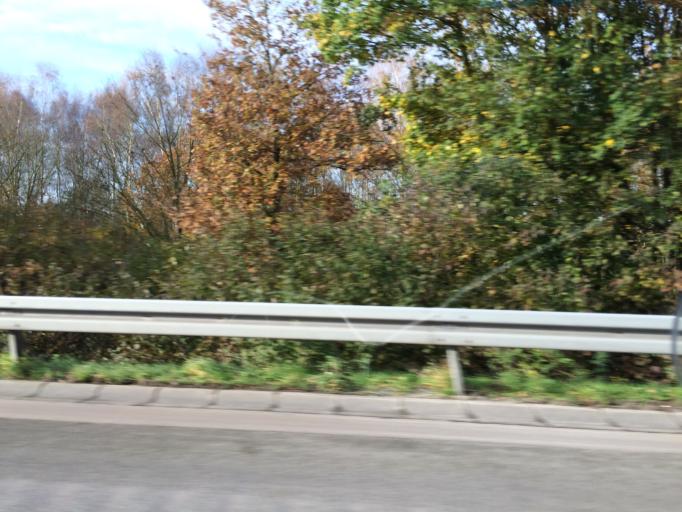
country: DE
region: North Rhine-Westphalia
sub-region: Regierungsbezirk Munster
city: Dulmen
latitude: 51.8315
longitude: 7.2379
